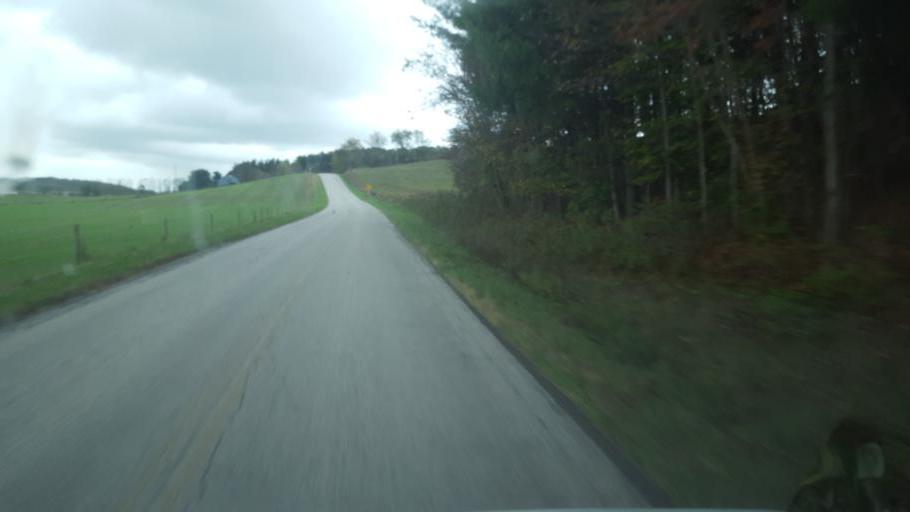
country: US
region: Ohio
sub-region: Ashland County
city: Loudonville
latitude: 40.6007
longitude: -82.1702
